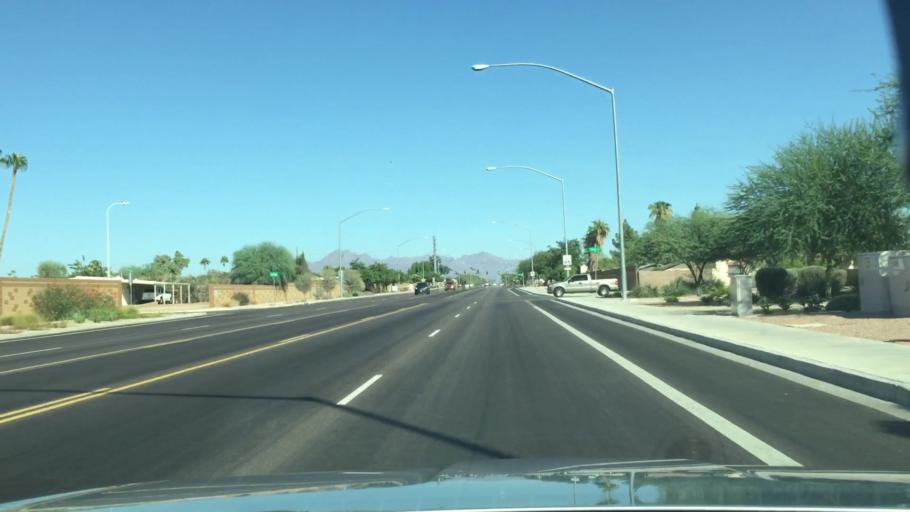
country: US
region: Arizona
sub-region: Pinal County
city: Apache Junction
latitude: 33.4079
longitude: -111.6719
